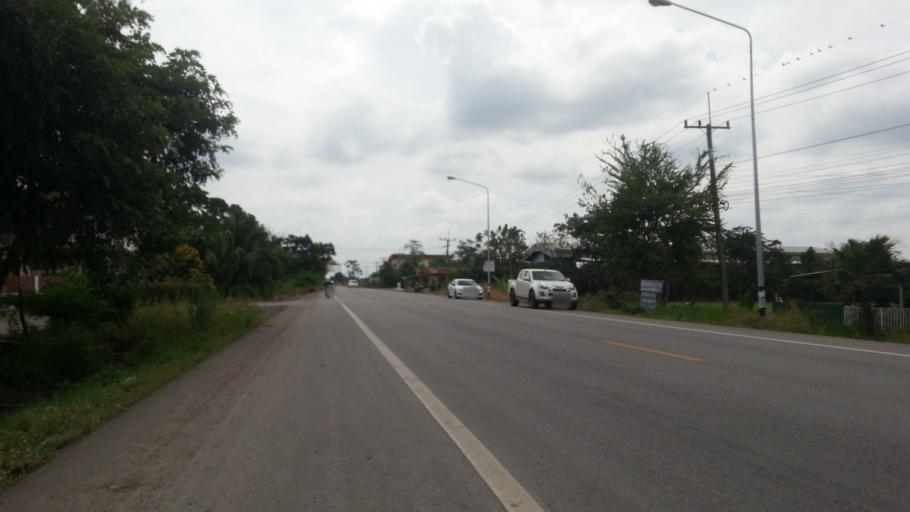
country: TH
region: Pathum Thani
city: Ban Lam Luk Ka
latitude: 14.0338
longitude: 100.8439
